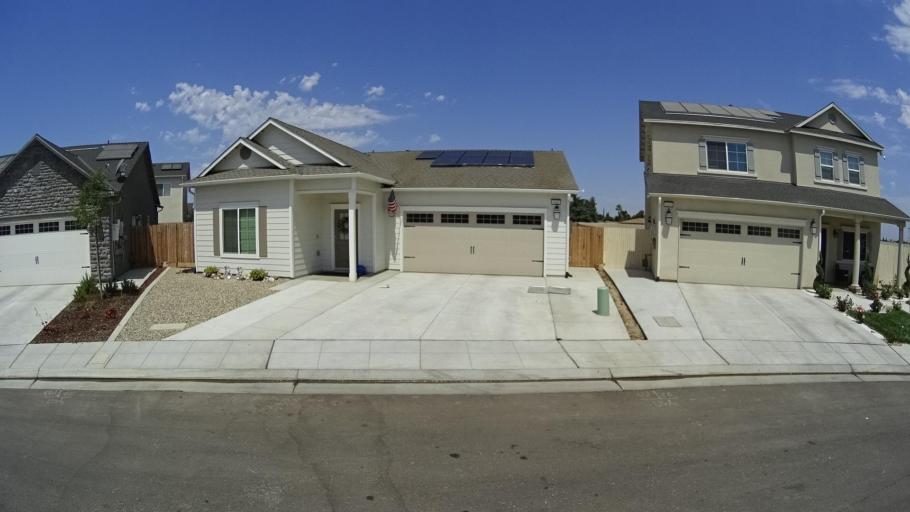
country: US
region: California
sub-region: Fresno County
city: Tarpey Village
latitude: 36.7841
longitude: -119.6807
